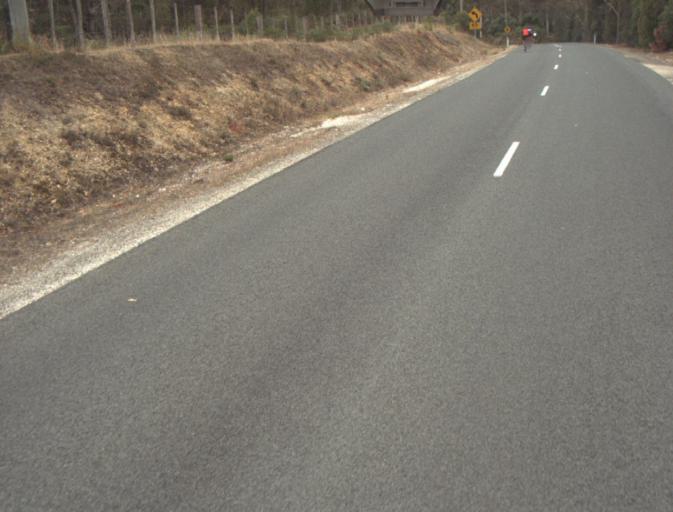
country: AU
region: Tasmania
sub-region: Dorset
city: Bridport
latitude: -41.1722
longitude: 147.2664
